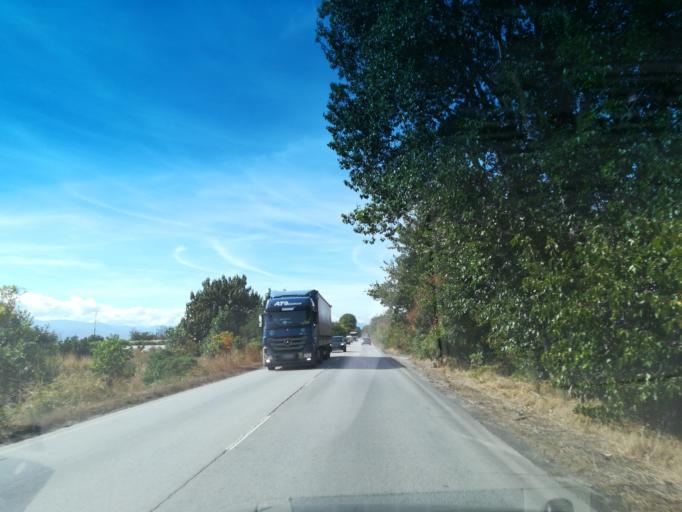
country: BG
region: Plovdiv
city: Stamboliyski
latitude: 42.1357
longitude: 24.6400
